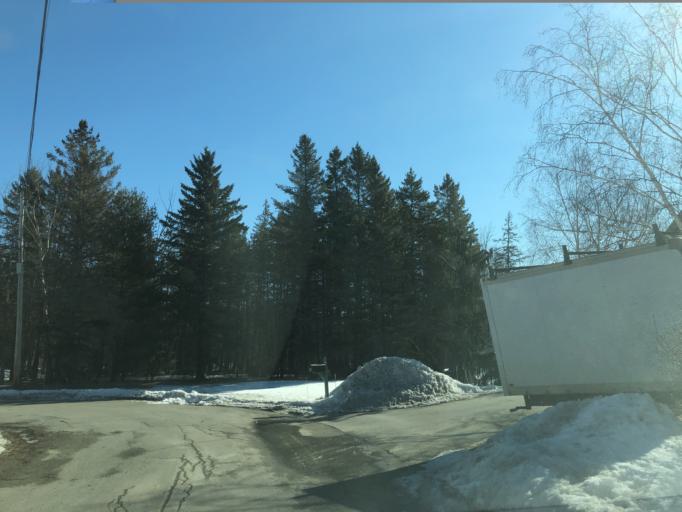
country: US
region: Maine
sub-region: Penobscot County
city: Brewer
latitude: 44.8186
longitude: -68.7516
